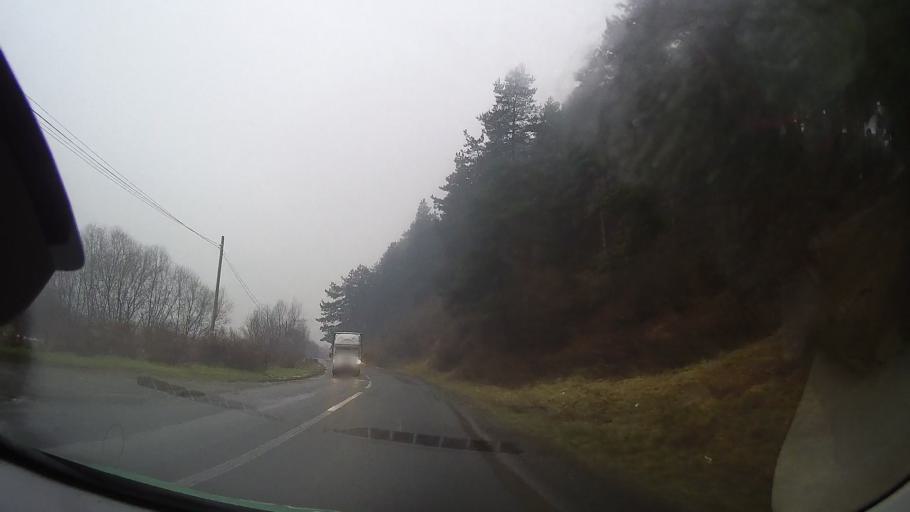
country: RO
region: Harghita
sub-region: Municipiul Gheorgheni
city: Gheorgheni
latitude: 46.7283
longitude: 25.6380
